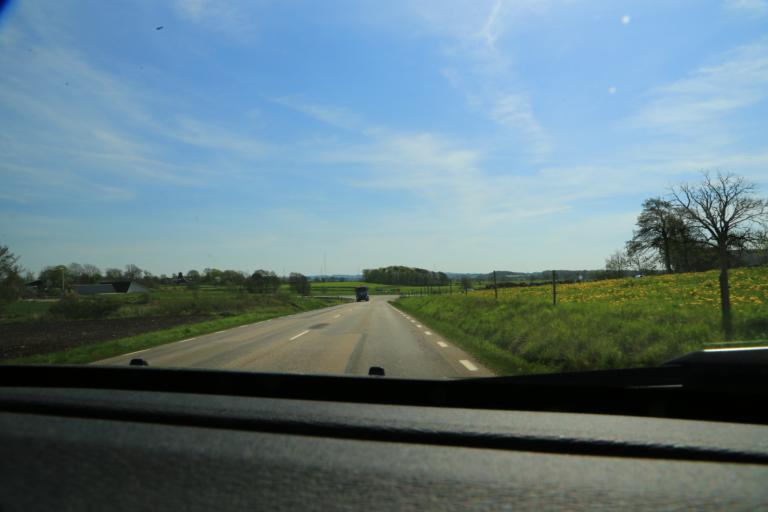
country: SE
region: Halland
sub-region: Varbergs Kommun
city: Varberg
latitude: 57.1331
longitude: 12.3187
